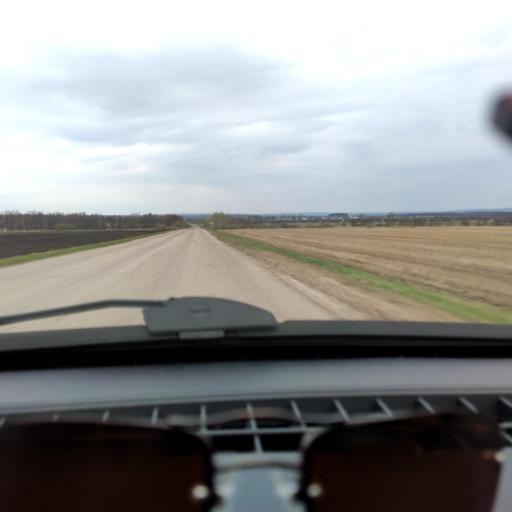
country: RU
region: Bashkortostan
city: Kabakovo
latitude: 54.4818
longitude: 56.1949
